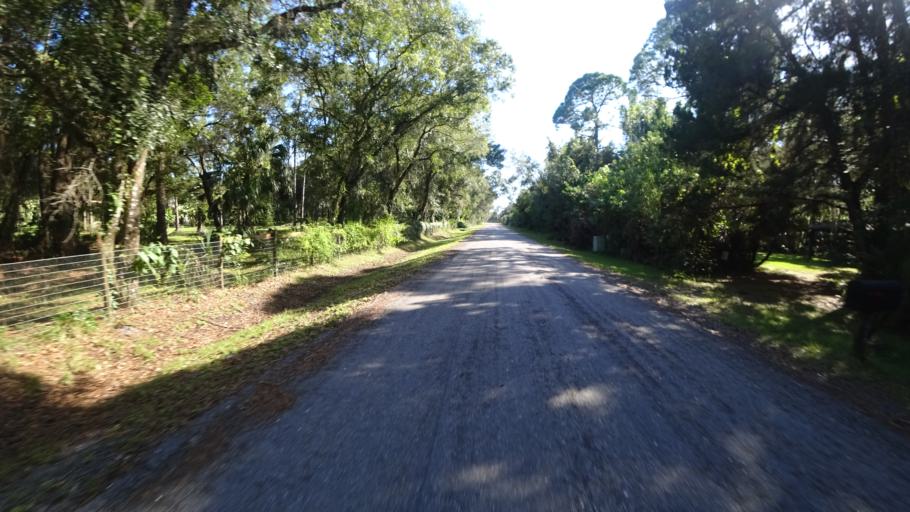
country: US
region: Florida
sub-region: Sarasota County
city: The Meadows
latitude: 27.4169
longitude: -82.4504
